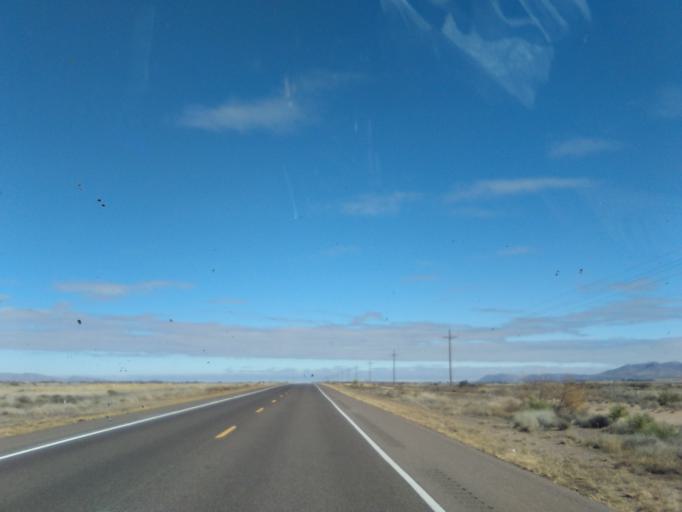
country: US
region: New Mexico
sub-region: Dona Ana County
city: Hatch
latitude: 32.5935
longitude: -107.3475
